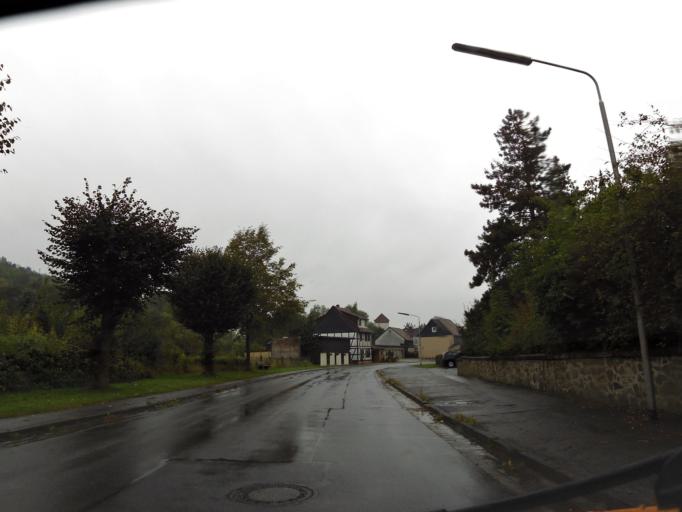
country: DE
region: Lower Saxony
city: Herzberg am Harz
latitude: 51.6267
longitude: 10.3870
